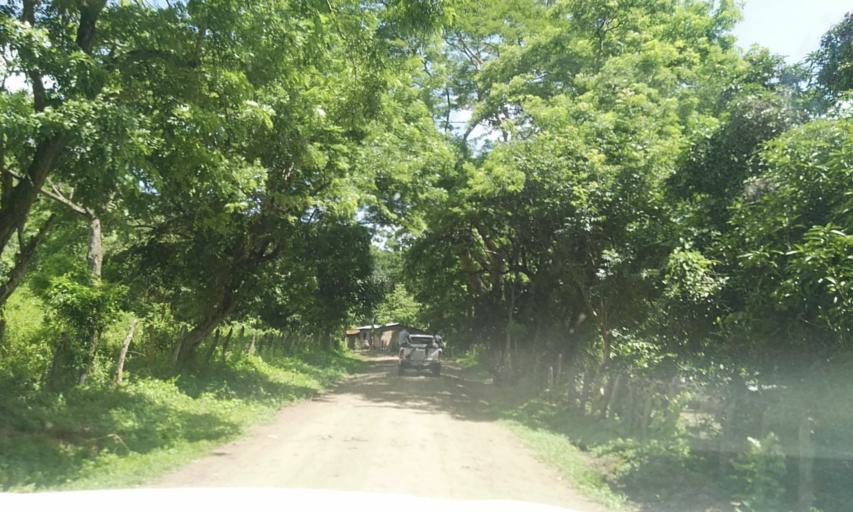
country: NI
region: Matagalpa
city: Terrabona
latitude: 12.7186
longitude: -85.9242
